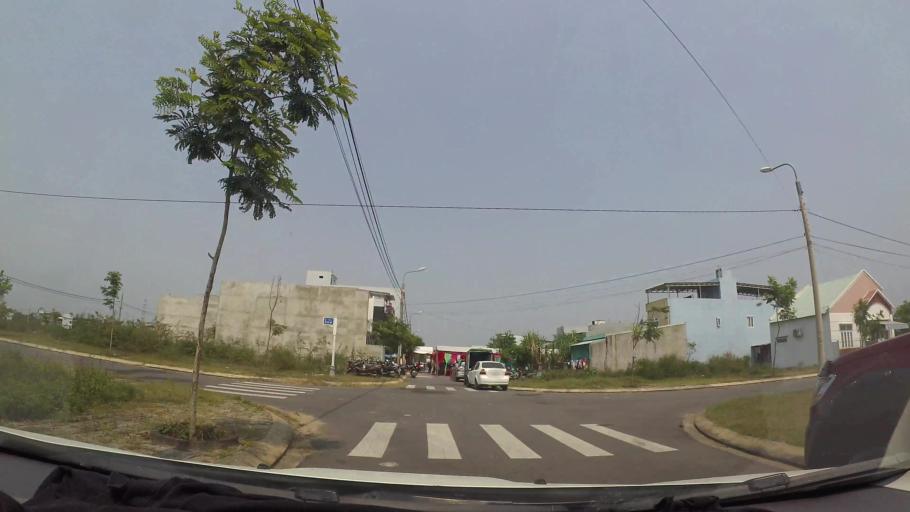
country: VN
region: Da Nang
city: Cam Le
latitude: 15.9899
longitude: 108.2024
